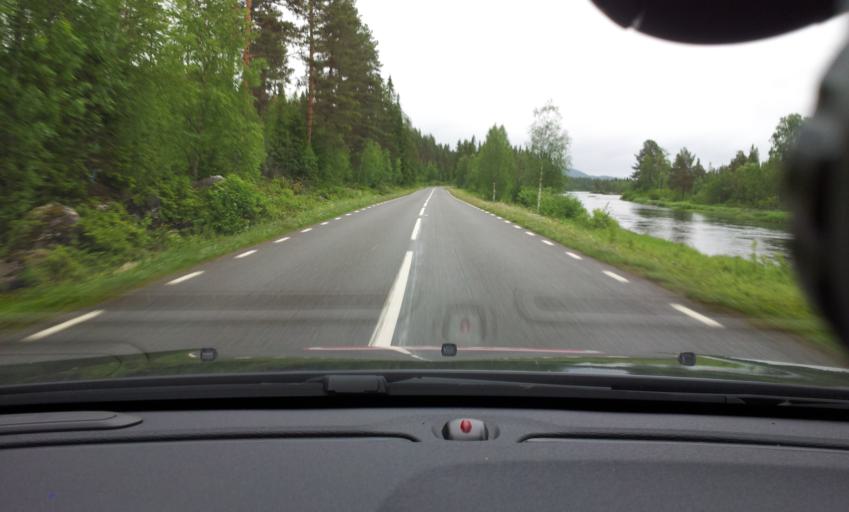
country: SE
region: Jaemtland
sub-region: Stroemsunds Kommun
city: Stroemsund
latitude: 63.4243
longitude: 15.5172
